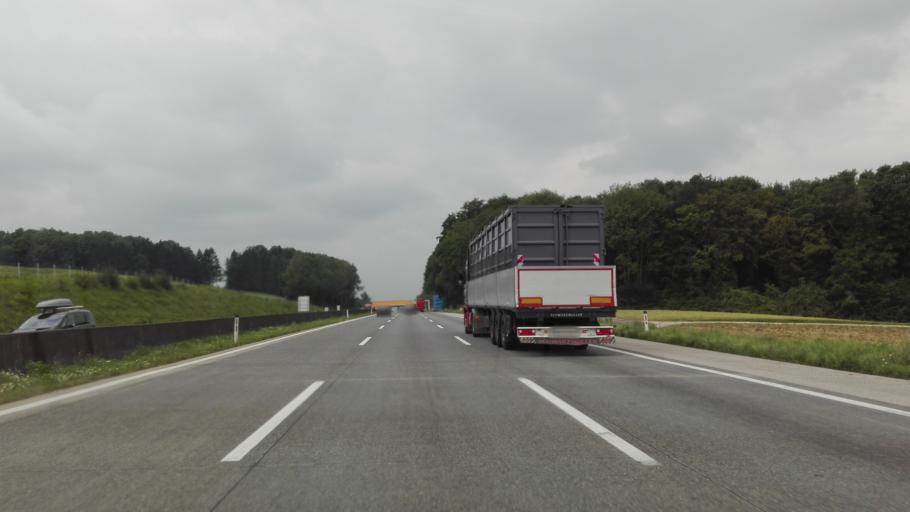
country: AT
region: Lower Austria
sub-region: Politischer Bezirk Scheibbs
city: Wieselburg
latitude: 48.1618
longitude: 15.1375
